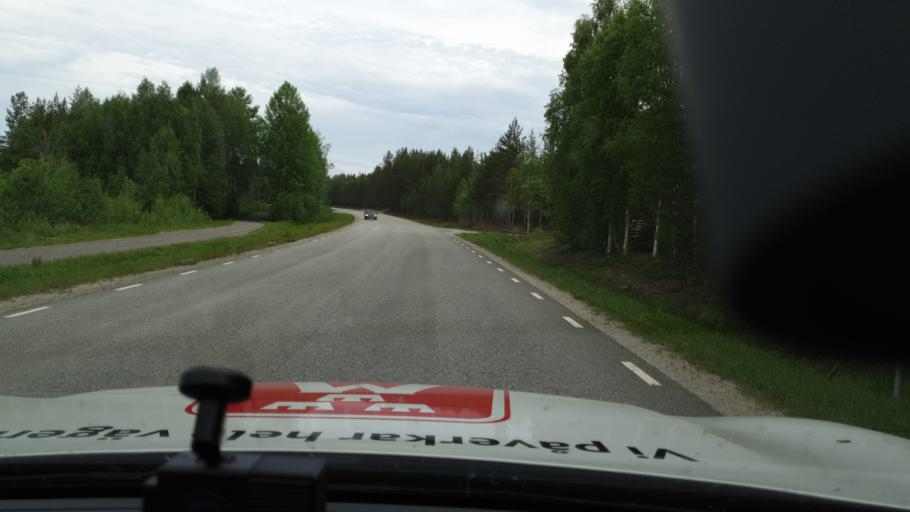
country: SE
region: Vaesterbotten
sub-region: Lycksele Kommun
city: Lycksele
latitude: 64.6099
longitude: 18.6974
